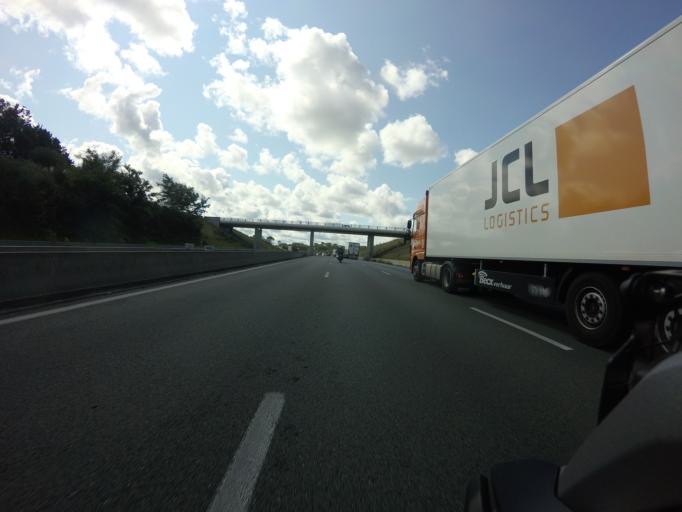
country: FR
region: Aquitaine
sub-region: Departement des Pyrenees-Atlantiques
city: Boucau
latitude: 43.5257
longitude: -1.4393
